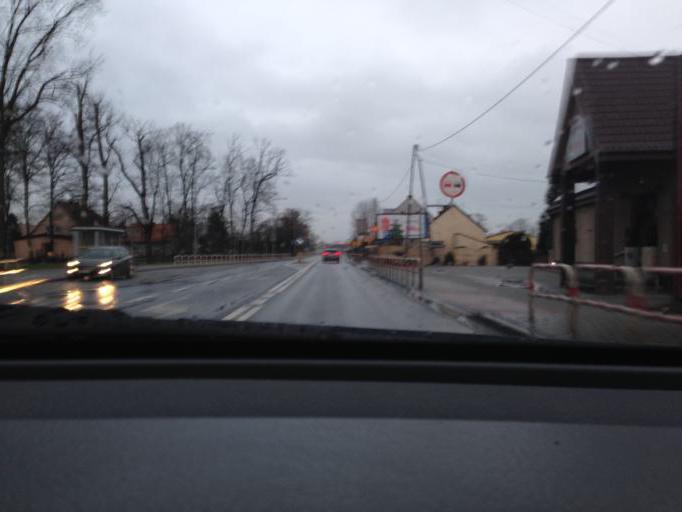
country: PL
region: Opole Voivodeship
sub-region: Powiat opolski
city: Wegry
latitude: 50.7137
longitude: 17.9936
